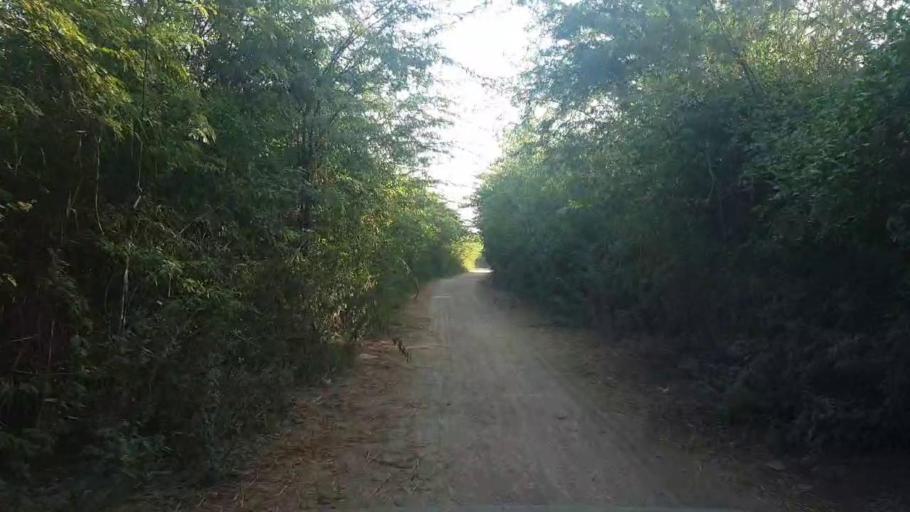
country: PK
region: Sindh
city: Tando Bago
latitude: 24.7408
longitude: 68.8913
